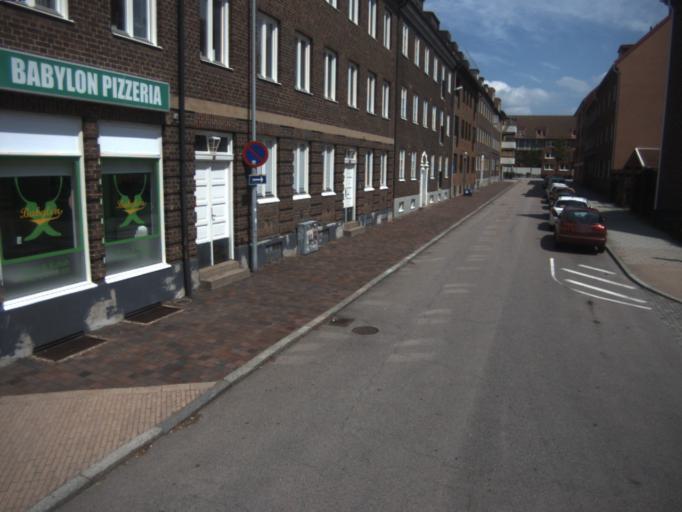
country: SE
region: Skane
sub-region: Helsingborg
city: Helsingborg
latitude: 56.0396
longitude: 12.7101
